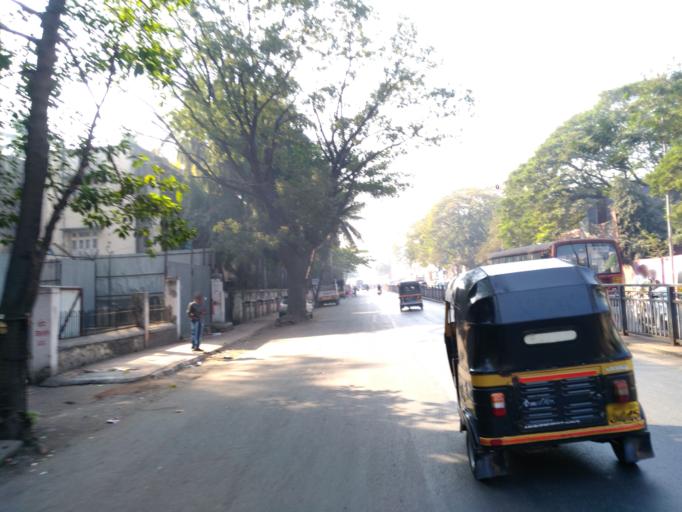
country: IN
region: Maharashtra
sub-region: Pune Division
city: Pune
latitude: 18.5051
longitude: 73.8687
